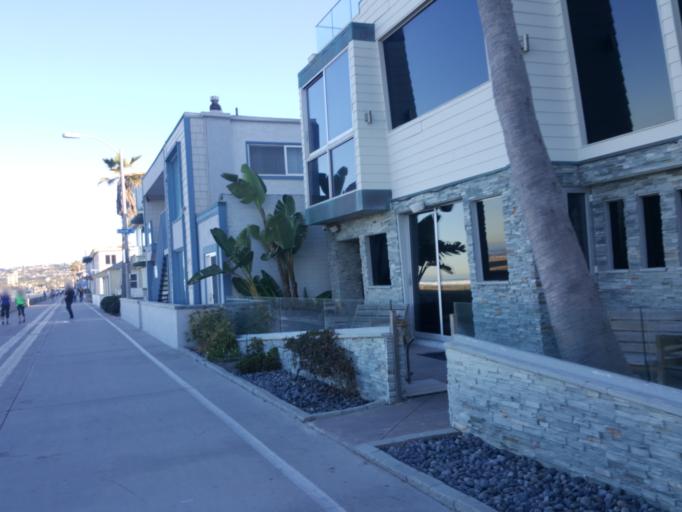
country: US
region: California
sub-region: San Diego County
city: La Jolla
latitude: 32.7846
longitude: -117.2539
